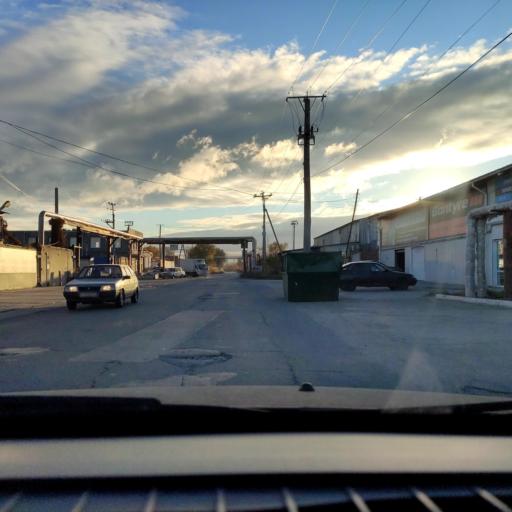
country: RU
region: Samara
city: Tol'yatti
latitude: 53.5756
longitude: 49.2810
